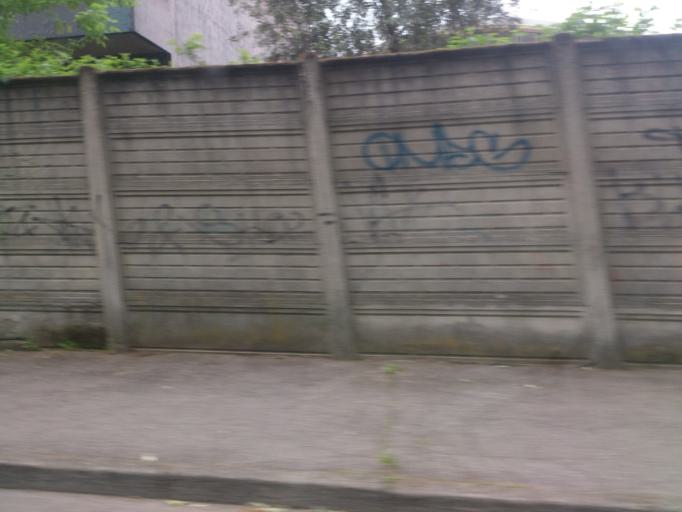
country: IT
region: Lombardy
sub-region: Citta metropolitana di Milano
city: Cologno Monzese
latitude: 45.5209
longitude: 9.2723
